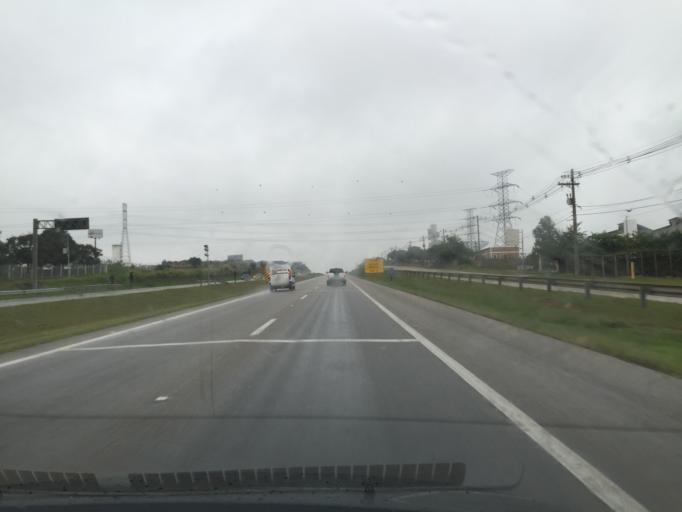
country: BR
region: Sao Paulo
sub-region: Itu
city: Itu
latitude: -23.3189
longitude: -47.3284
